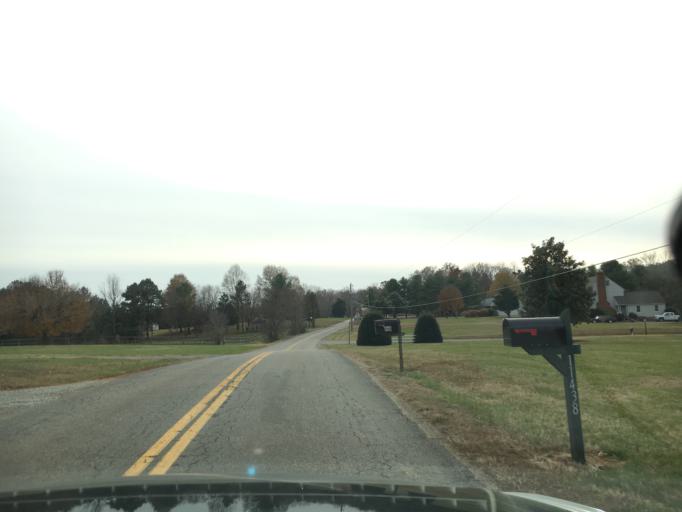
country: US
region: Virginia
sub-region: Henrico County
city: Wyndham
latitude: 37.7243
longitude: -77.6793
